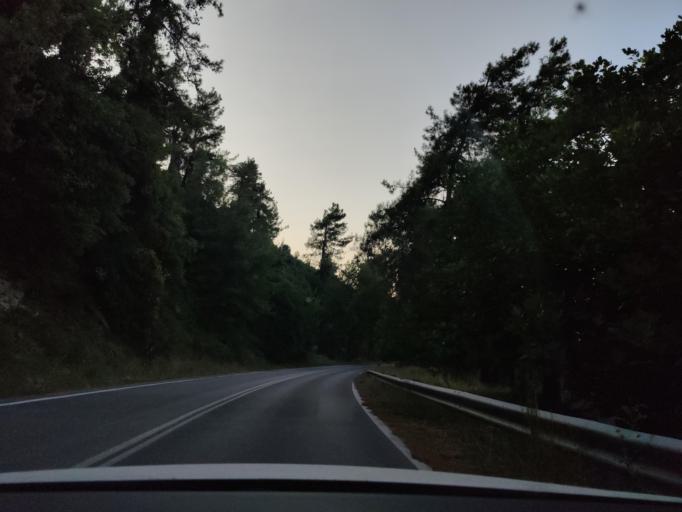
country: GR
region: East Macedonia and Thrace
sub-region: Nomos Kavalas
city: Potamia
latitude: 40.7059
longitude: 24.7672
